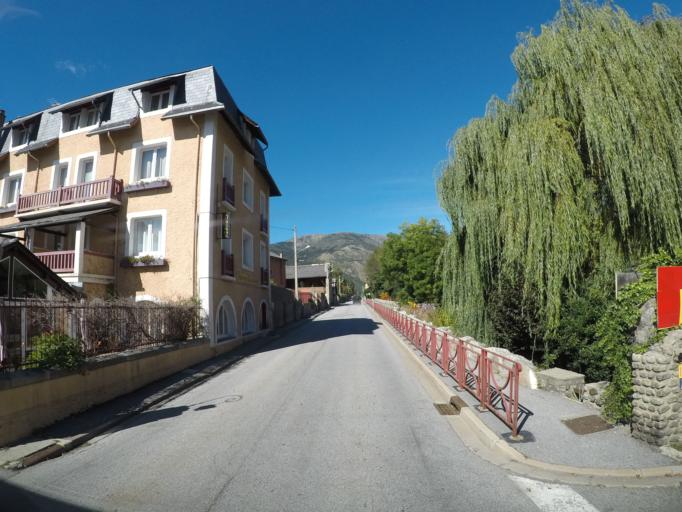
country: ES
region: Catalonia
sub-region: Provincia de Girona
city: Guils de Cerdanya
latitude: 42.4652
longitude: 1.8903
